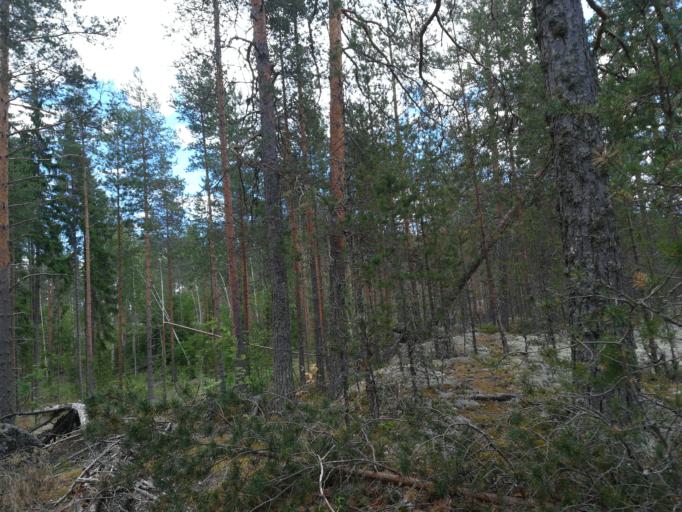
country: FI
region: Southern Savonia
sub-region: Mikkeli
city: Hirvensalmi
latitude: 61.7082
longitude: 26.9711
